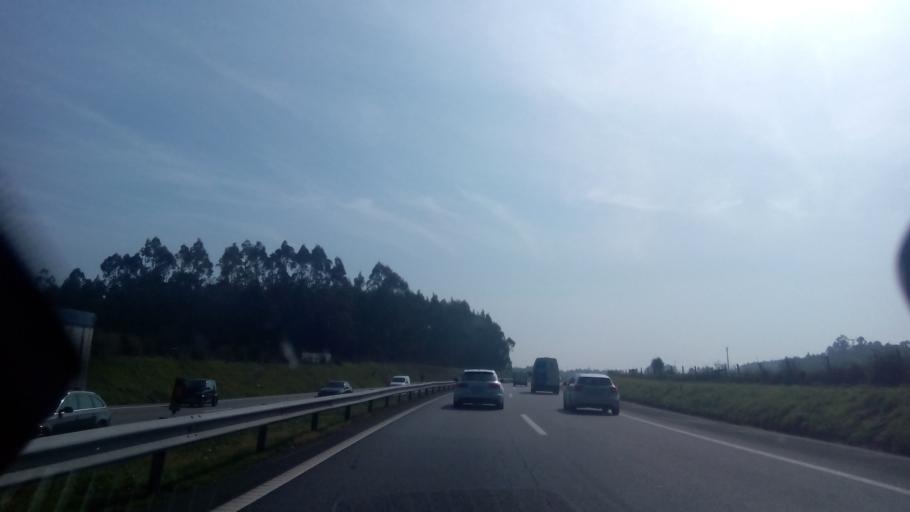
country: PT
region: Porto
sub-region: Vila do Conde
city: Arvore
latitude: 41.3577
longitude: -8.7146
